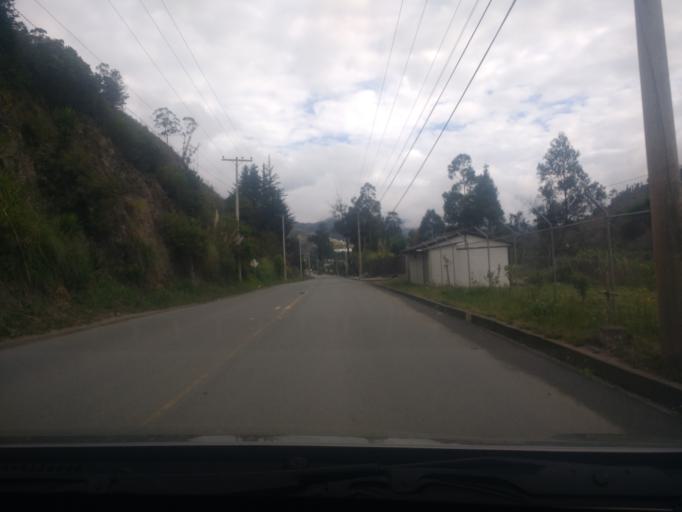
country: EC
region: Azuay
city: La Union
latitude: -2.8215
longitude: -78.7725
